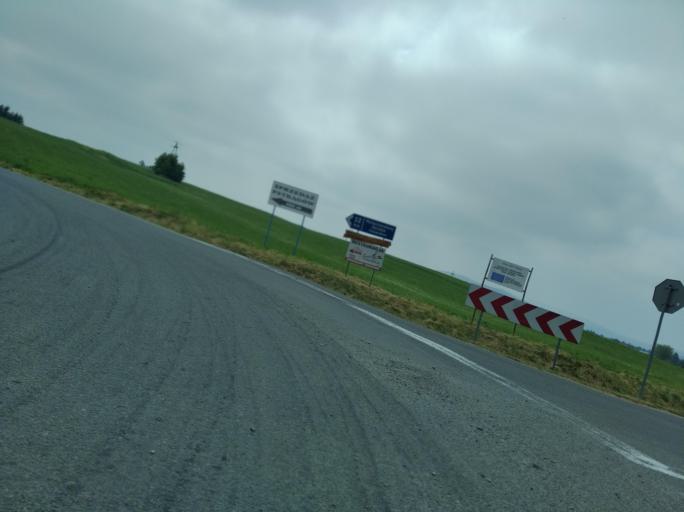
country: PL
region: Subcarpathian Voivodeship
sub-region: Powiat krosnienski
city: Sieniawa
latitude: 49.5648
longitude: 21.9233
